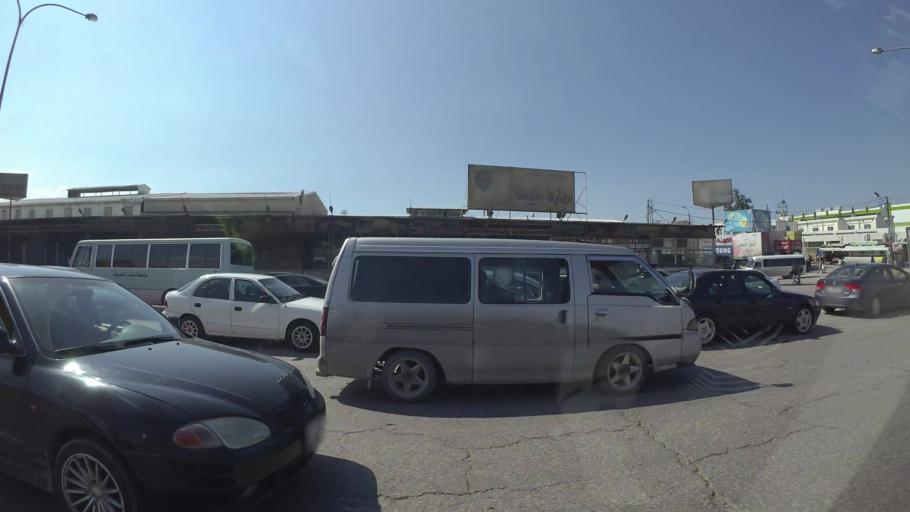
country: JO
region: Zarqa
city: Zarqa
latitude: 32.0558
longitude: 36.0949
